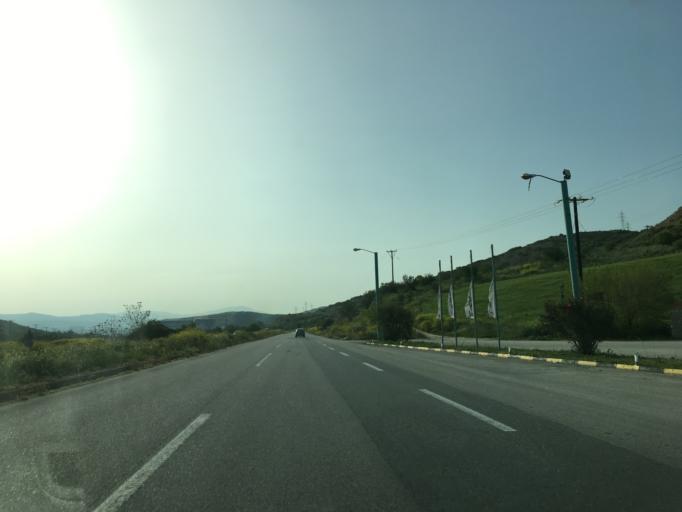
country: GR
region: Thessaly
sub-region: Nomos Magnisias
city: Velestino
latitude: 39.3823
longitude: 22.8243
